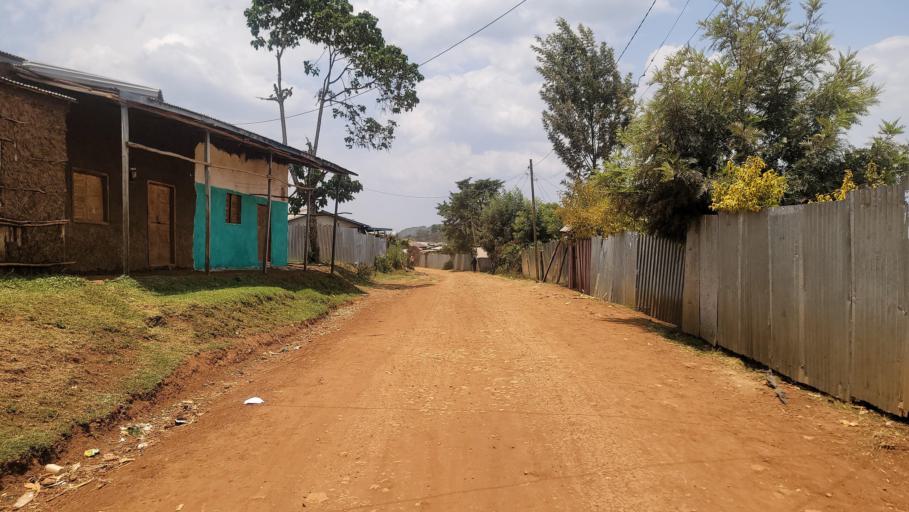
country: ET
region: Oromiya
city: Agaro
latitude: 7.7943
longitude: 36.4778
